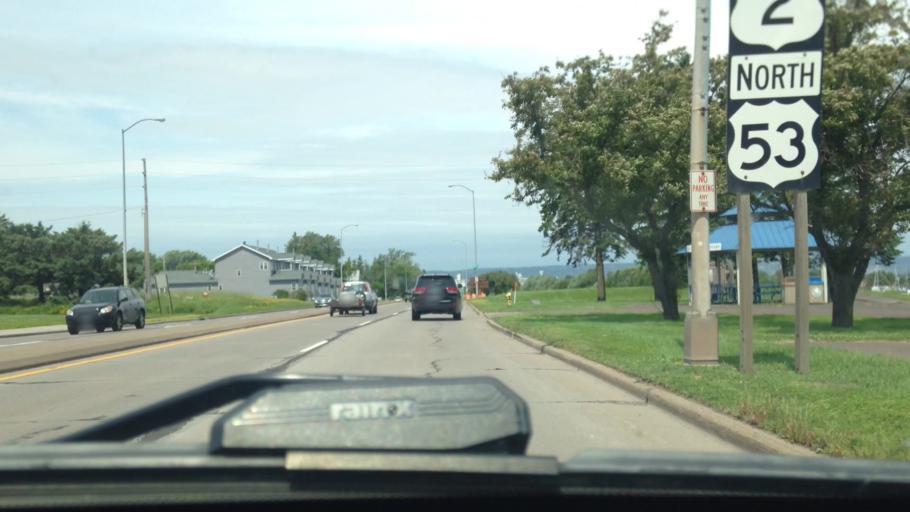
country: US
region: Wisconsin
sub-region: Douglas County
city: Superior
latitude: 46.7114
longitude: -92.0533
